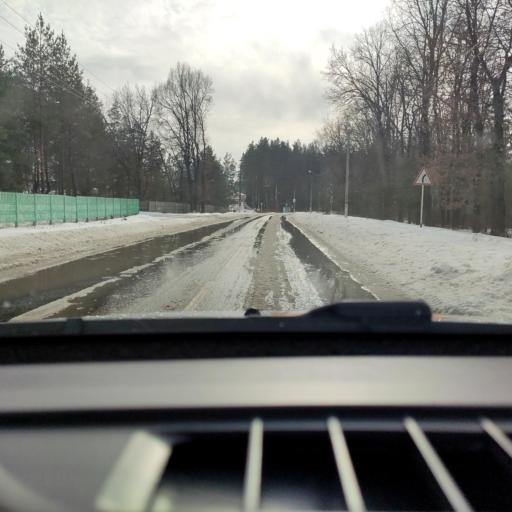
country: RU
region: Voronezj
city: Podgornoye
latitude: 51.7872
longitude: 39.1461
